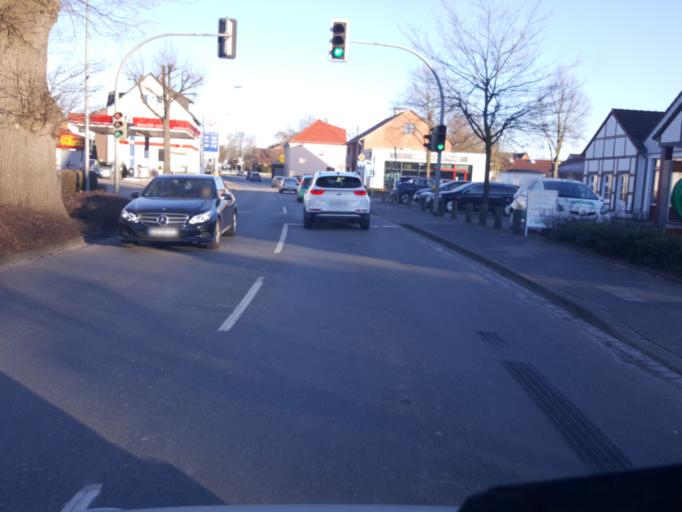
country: DE
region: North Rhine-Westphalia
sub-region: Regierungsbezirk Detmold
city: Hille
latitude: 52.3364
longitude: 8.7446
